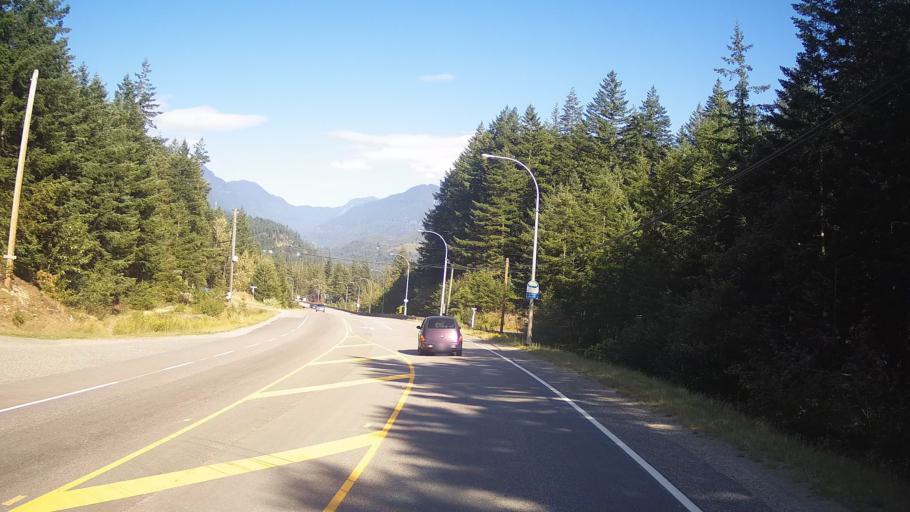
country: CA
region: British Columbia
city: Hope
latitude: 49.3863
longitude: -121.4586
